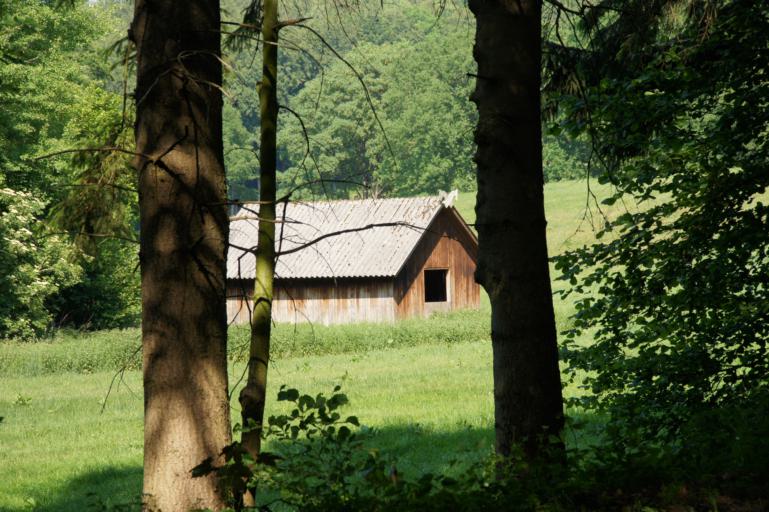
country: DE
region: Schleswig-Holstein
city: Malente
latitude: 54.1714
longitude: 10.5403
